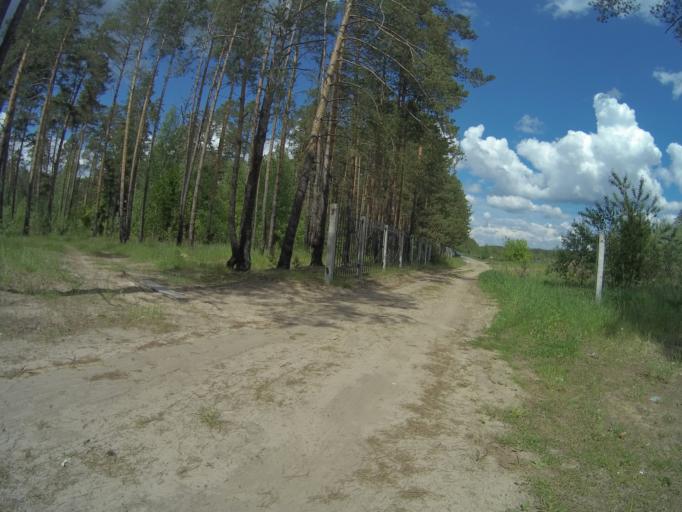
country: RU
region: Vladimir
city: Golovino
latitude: 56.0261
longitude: 40.4173
